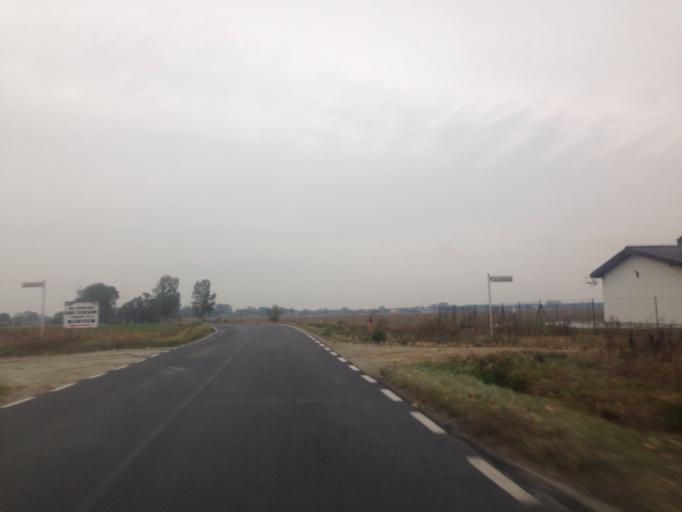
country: PL
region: Greater Poland Voivodeship
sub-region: Powiat poznanski
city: Swarzedz
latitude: 52.3486
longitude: 17.0993
